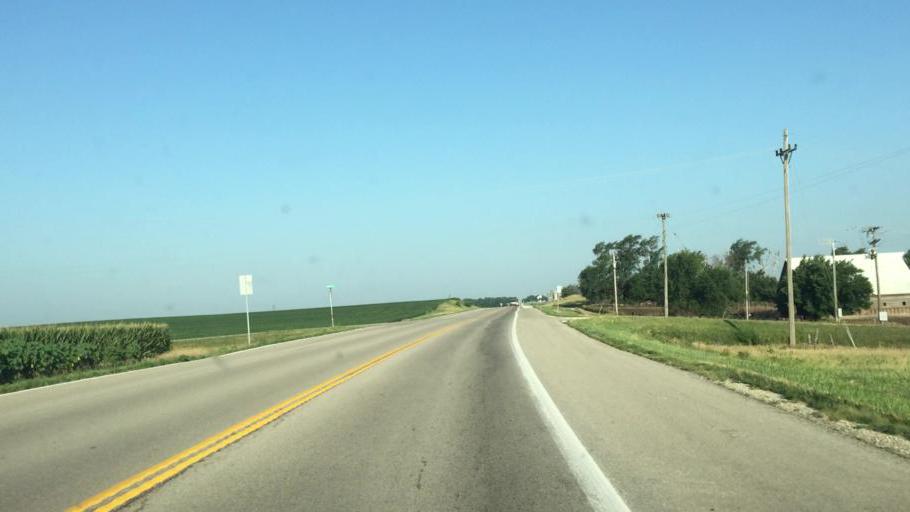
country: US
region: Kansas
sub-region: Nemaha County
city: Sabetha
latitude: 39.8411
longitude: -95.6945
